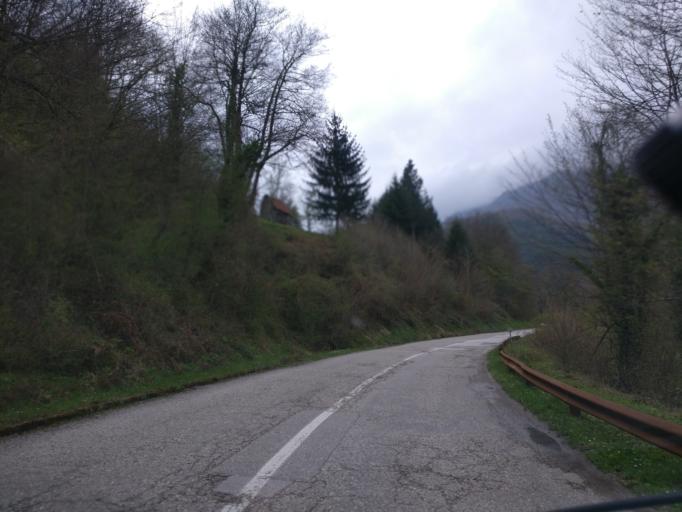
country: BA
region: Republika Srpska
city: Foca
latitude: 43.4617
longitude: 18.7475
